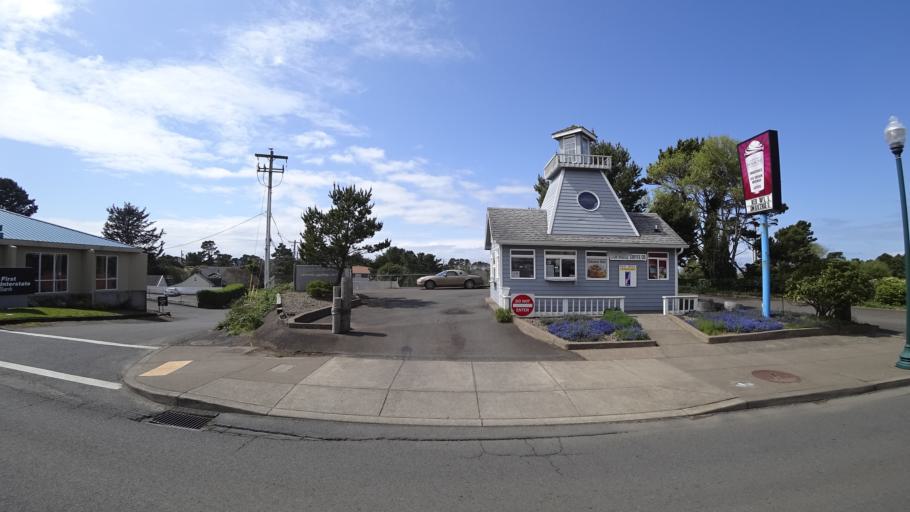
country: US
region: Oregon
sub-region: Lincoln County
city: Lincoln City
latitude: 44.9792
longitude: -124.0105
